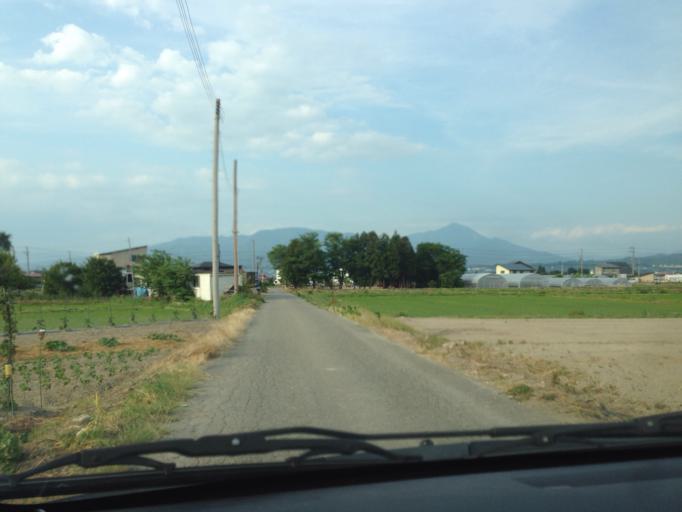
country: JP
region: Fukushima
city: Kitakata
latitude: 37.5208
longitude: 139.8923
